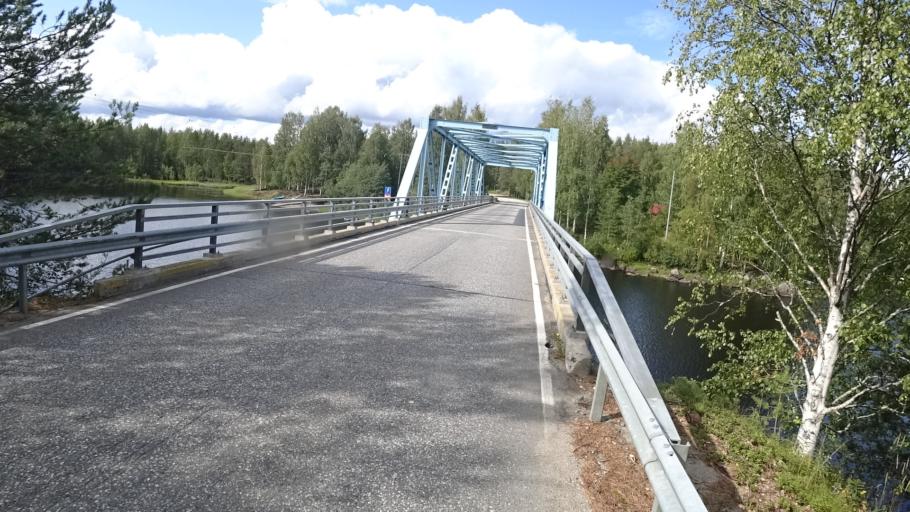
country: FI
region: North Karelia
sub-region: Joensuu
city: Ilomantsi
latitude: 62.6214
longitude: 31.1989
